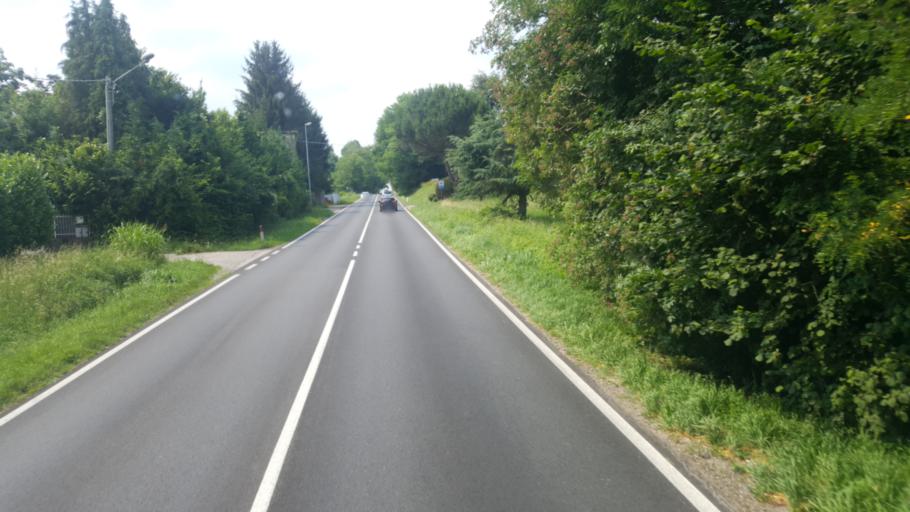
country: IT
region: Lombardy
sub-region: Provincia di Como
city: Oltrona di San Mamette
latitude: 45.7592
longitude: 8.9651
